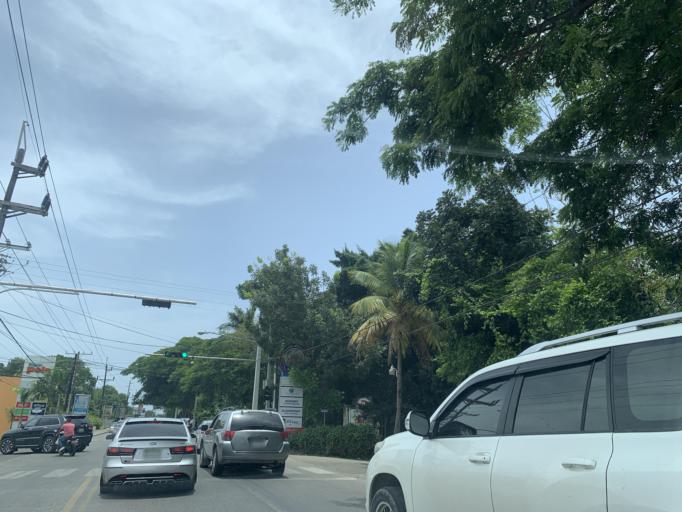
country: DO
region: Puerto Plata
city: Cabarete
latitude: 19.7667
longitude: -70.5074
